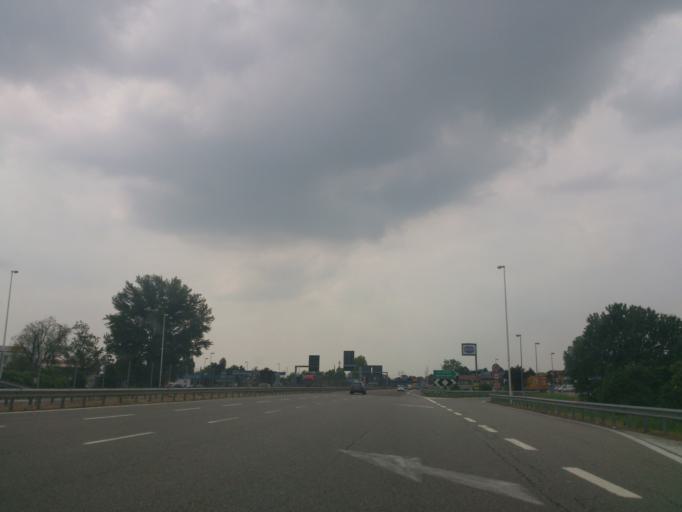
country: IT
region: Lombardy
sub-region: Citta metropolitana di Milano
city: Carugate
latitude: 45.5599
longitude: 9.3322
